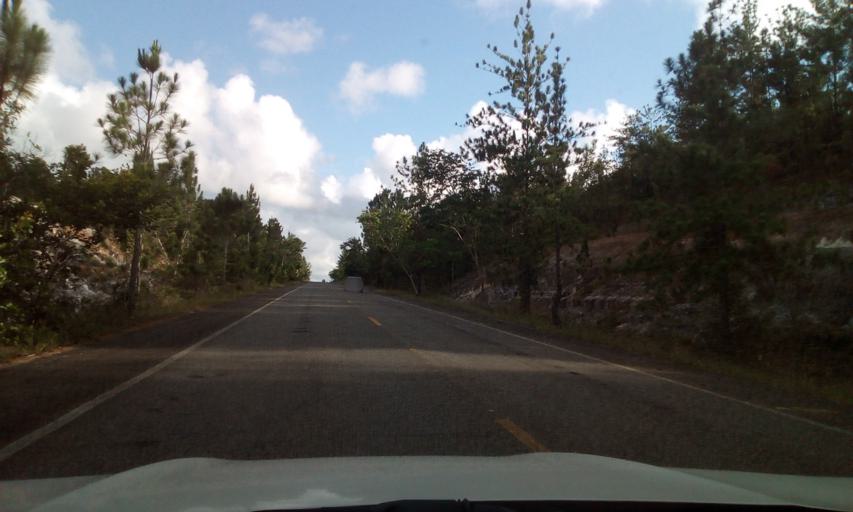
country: BR
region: Bahia
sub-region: Entre Rios
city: Entre Rios
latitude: -12.1258
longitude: -37.7903
